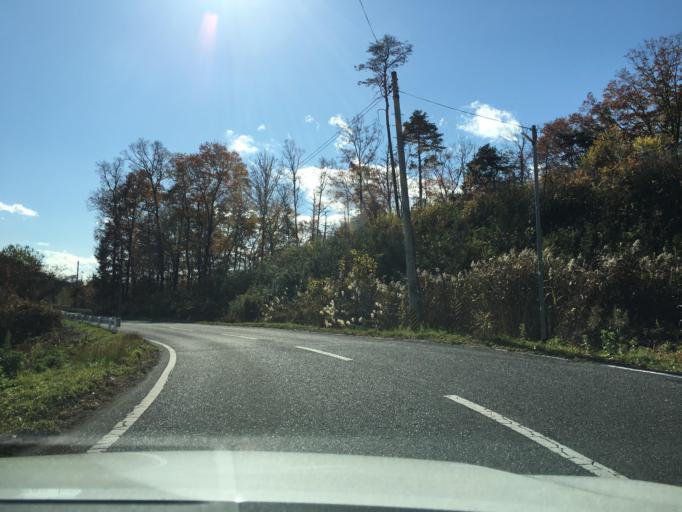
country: JP
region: Fukushima
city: Motomiya
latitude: 37.4715
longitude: 140.4231
